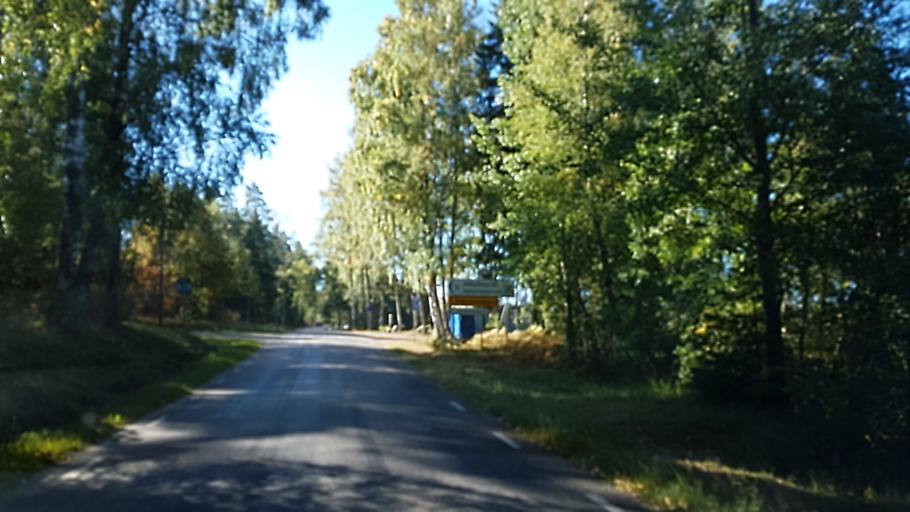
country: SE
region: Kronoberg
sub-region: Ljungby Kommun
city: Ljungby
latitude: 56.8010
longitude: 14.0326
